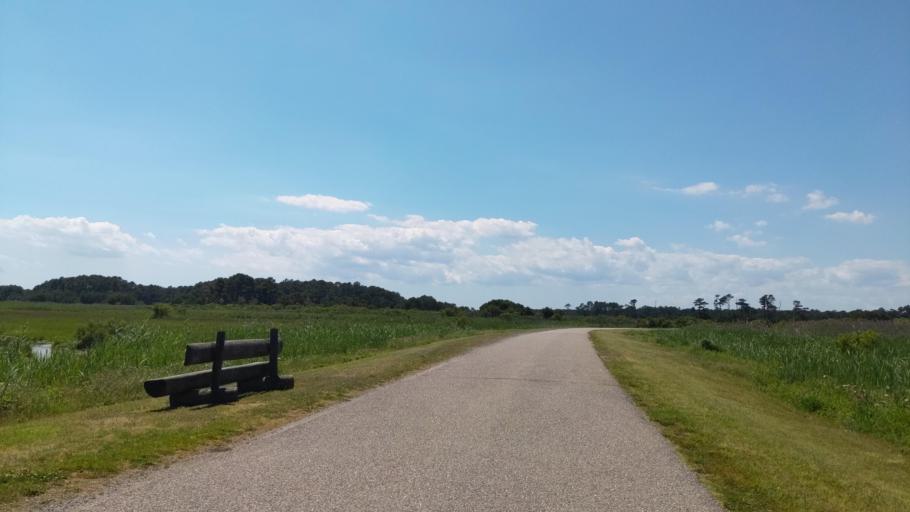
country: US
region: Virginia
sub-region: Accomack County
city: Chincoteague
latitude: 37.9019
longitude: -75.3481
